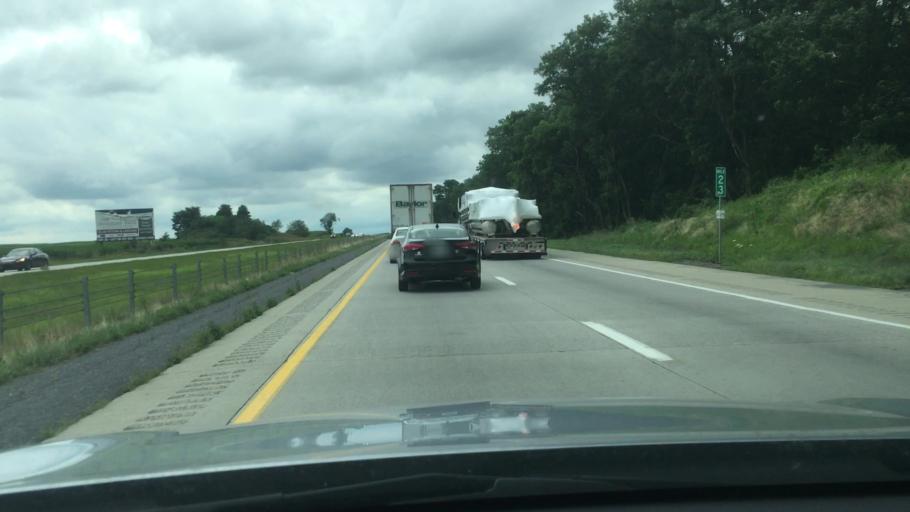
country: US
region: Pennsylvania
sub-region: Franklin County
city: Scotland
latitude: 40.0031
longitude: -77.5494
